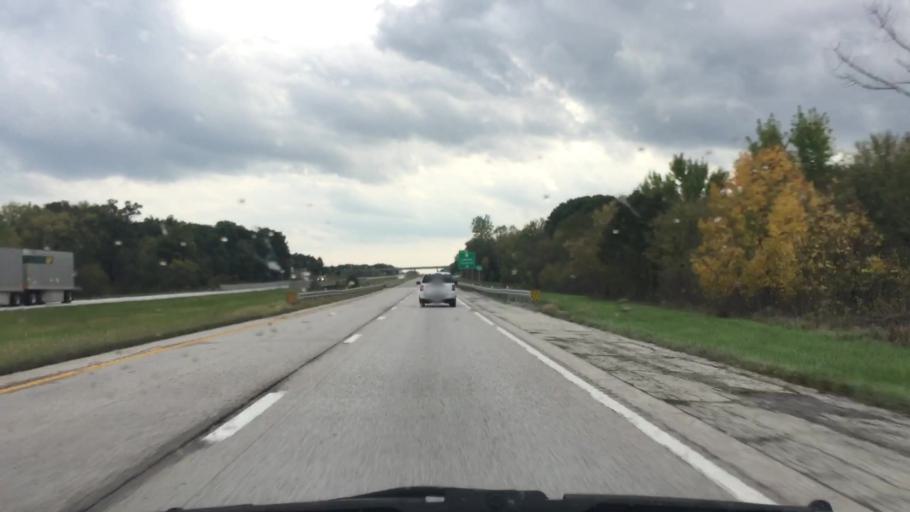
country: US
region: Missouri
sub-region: Clinton County
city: Cameron
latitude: 39.6755
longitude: -94.2340
